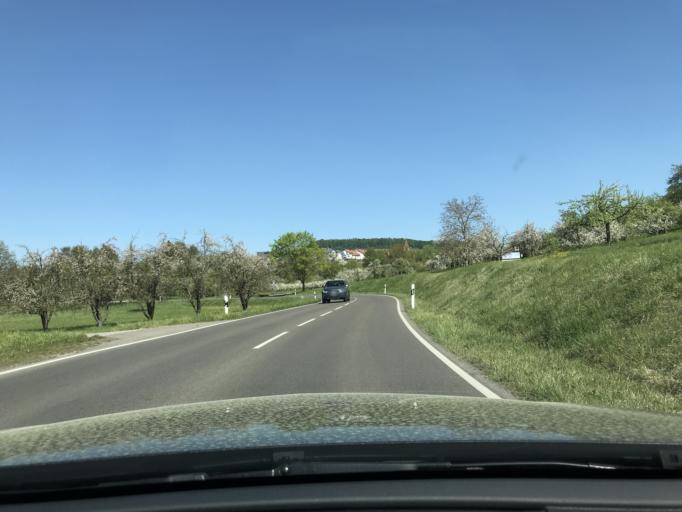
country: DE
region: Baden-Wuerttemberg
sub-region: Regierungsbezirk Stuttgart
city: Korb
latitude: 48.8330
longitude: 9.3708
